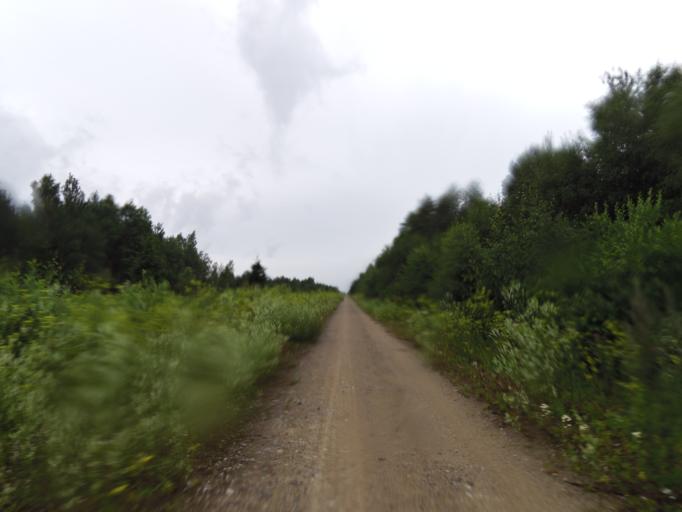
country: EE
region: Laeaene
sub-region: Ridala Parish
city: Uuemoisa
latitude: 58.9561
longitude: 23.8466
